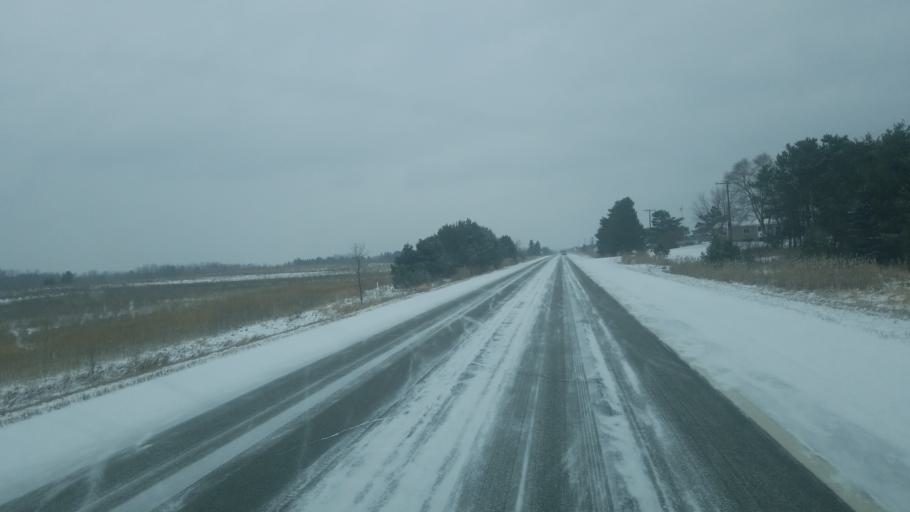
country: US
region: Michigan
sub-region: Osceola County
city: Evart
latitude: 43.9252
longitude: -85.1484
